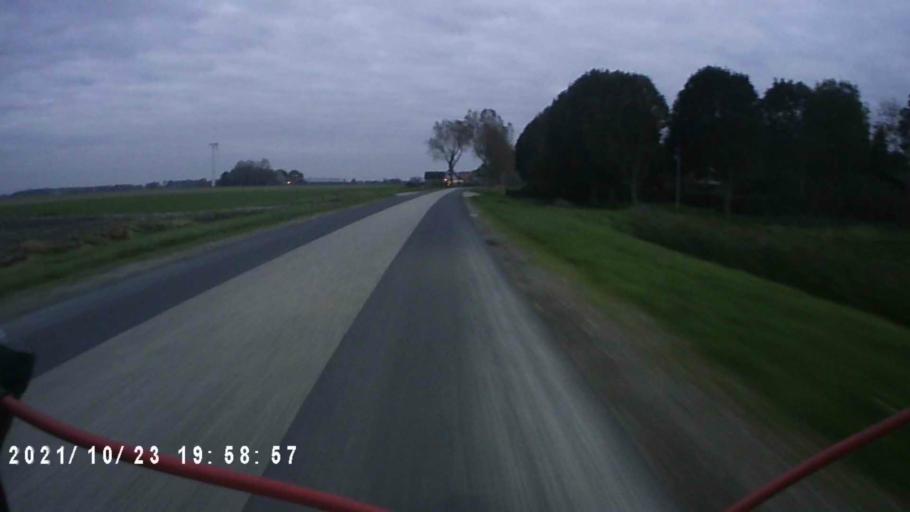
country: NL
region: Friesland
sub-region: Gemeente Harlingen
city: Harlingen
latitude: 53.1118
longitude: 5.4546
